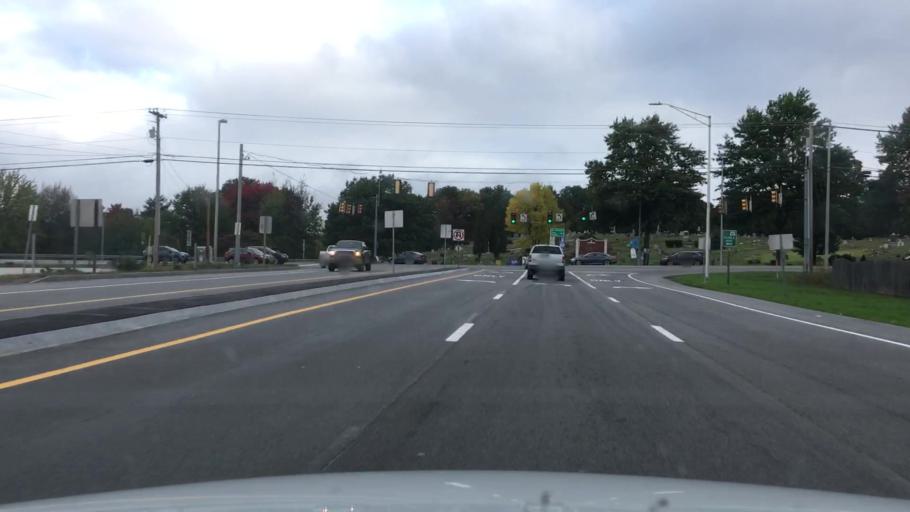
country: US
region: Maine
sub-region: Cumberland County
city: New Gloucester
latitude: 43.8833
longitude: -70.3333
